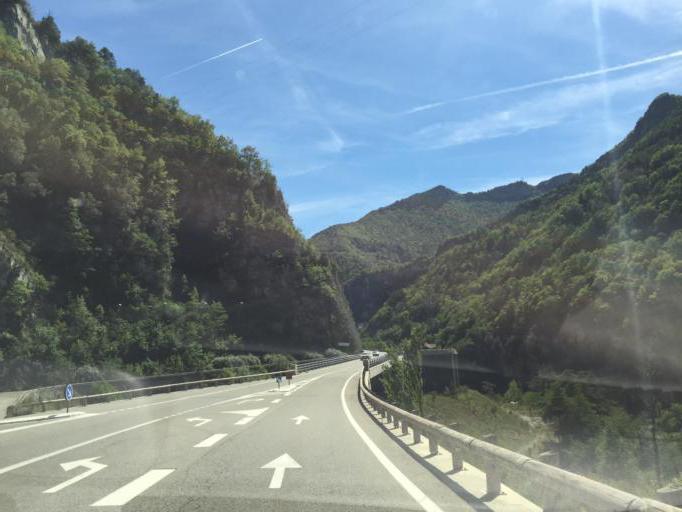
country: FR
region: Provence-Alpes-Cote d'Azur
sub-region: Departement des Alpes-Maritimes
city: Saint-Martin-Vesubie
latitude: 44.0464
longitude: 7.1296
